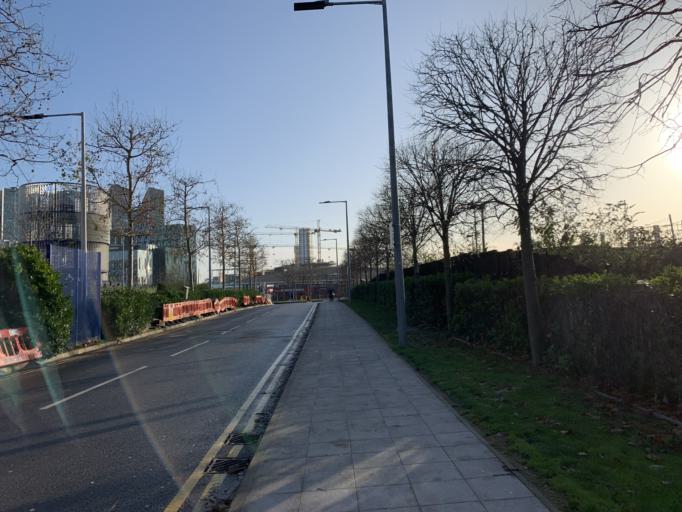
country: GB
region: England
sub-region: Greater London
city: Poplar
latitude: 51.5016
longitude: 0.0009
